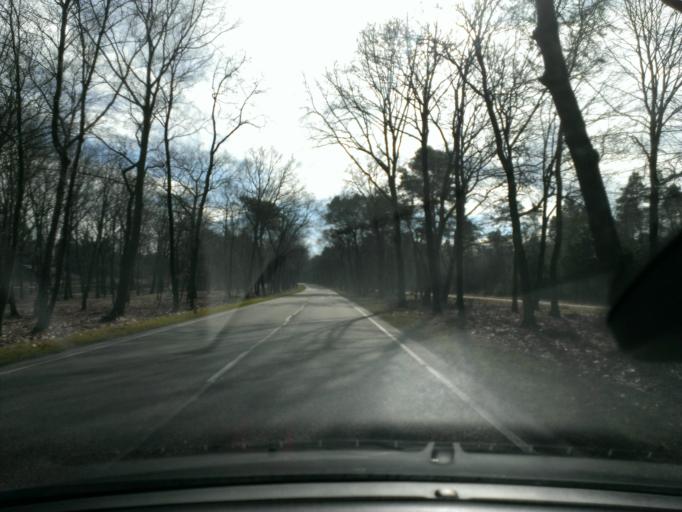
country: NL
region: Gelderland
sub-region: Gemeente Heerde
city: Heerde
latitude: 52.4231
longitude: 6.0129
